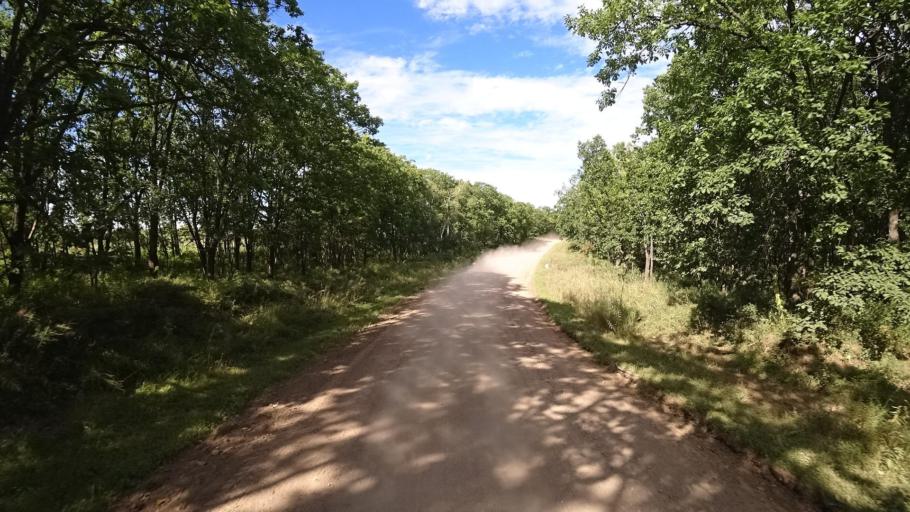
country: RU
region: Primorskiy
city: Yakovlevka
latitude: 44.4050
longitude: 133.5660
